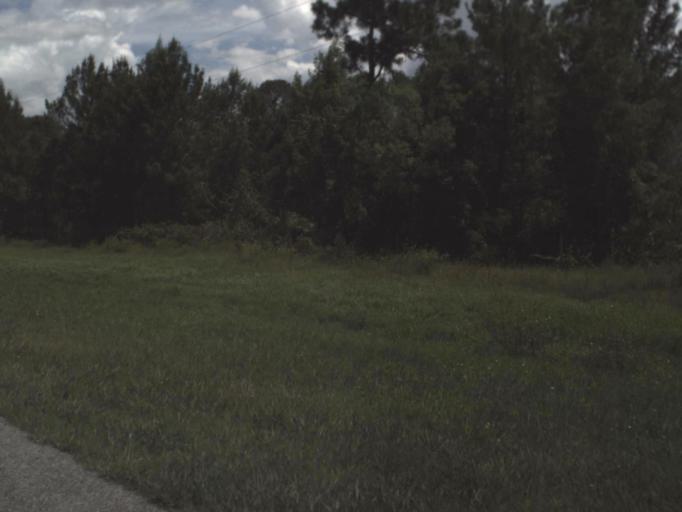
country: US
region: Florida
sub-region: Polk County
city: Babson Park
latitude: 27.8829
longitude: -81.4475
